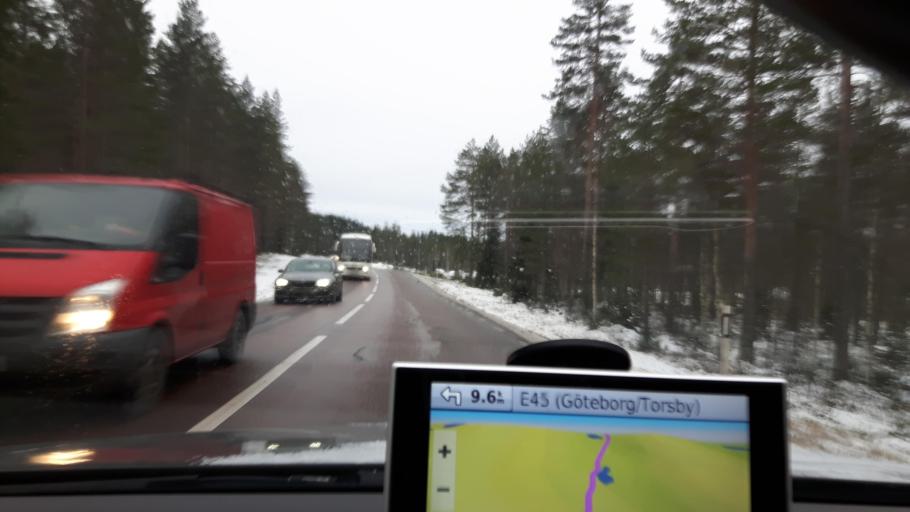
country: SE
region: Vaermland
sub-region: Torsby Kommun
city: Torsby
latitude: 60.3416
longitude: 13.1522
